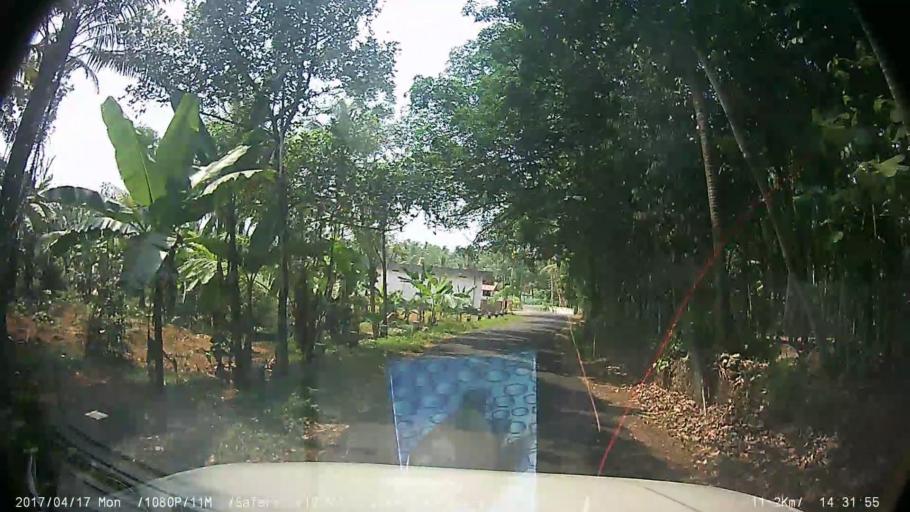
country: IN
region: Kerala
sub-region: Ernakulam
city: Piravam
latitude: 9.8174
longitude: 76.5529
